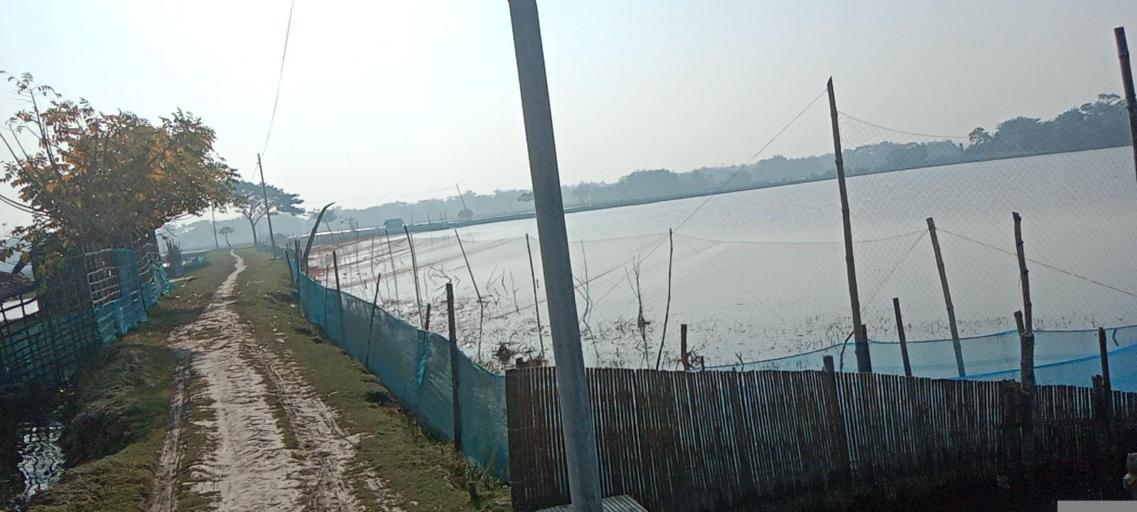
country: BD
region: Khulna
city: Phultala
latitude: 22.6109
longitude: 89.5845
